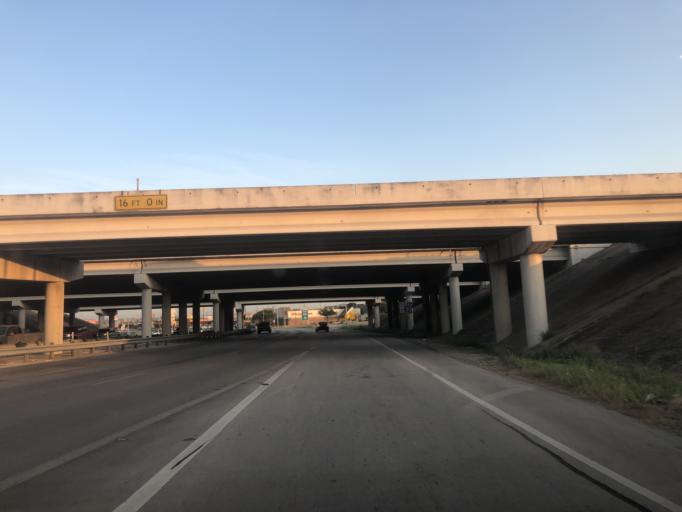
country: US
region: Texas
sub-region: Tarrant County
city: Sansom Park
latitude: 32.8087
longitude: -97.4178
